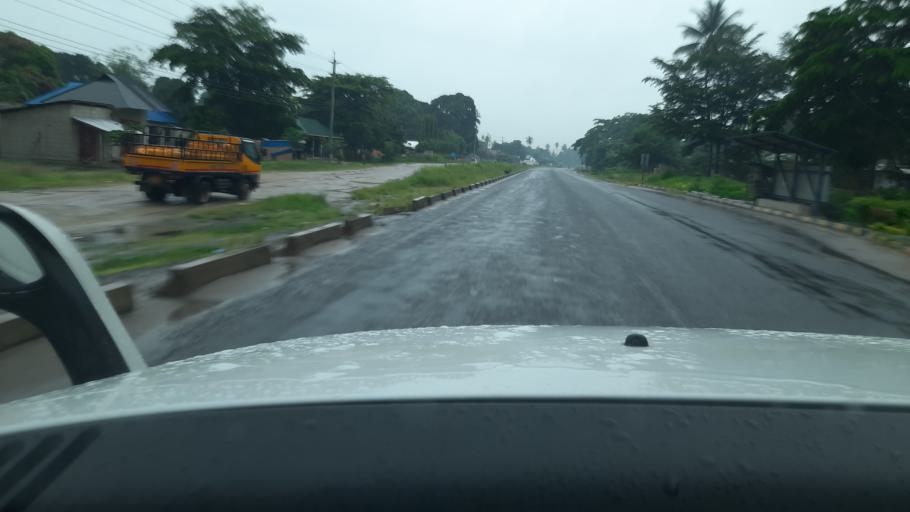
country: TZ
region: Pwani
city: Bagamoyo
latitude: -6.5099
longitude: 38.9350
